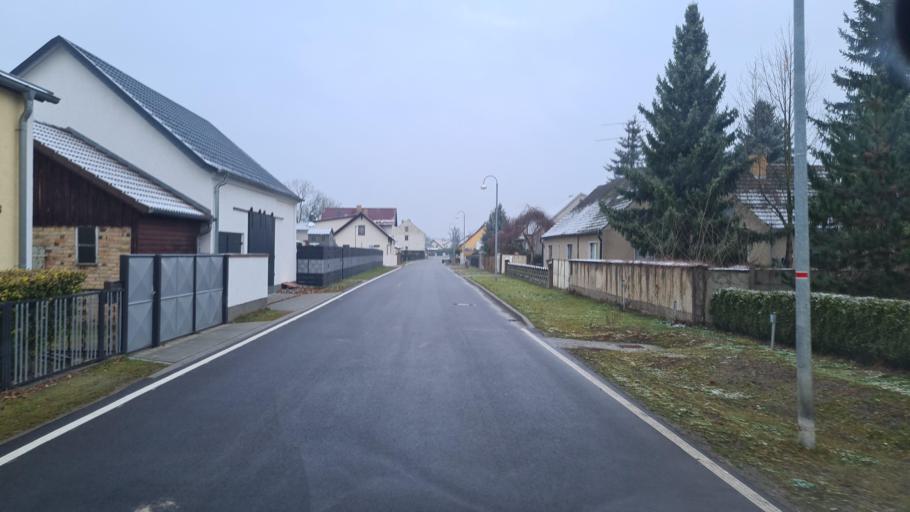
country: DE
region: Brandenburg
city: Storkow
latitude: 52.2866
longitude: 13.8805
